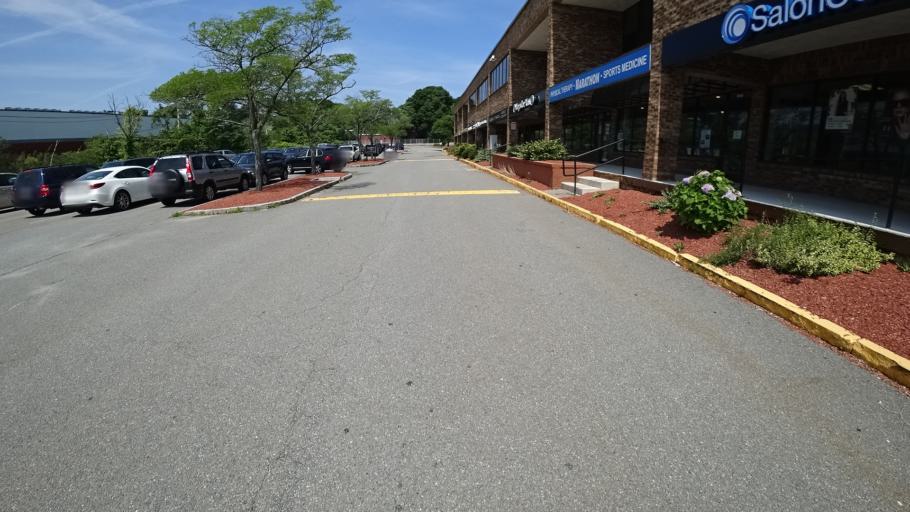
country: US
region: Massachusetts
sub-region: Norfolk County
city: Dedham
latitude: 42.2429
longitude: -71.1732
